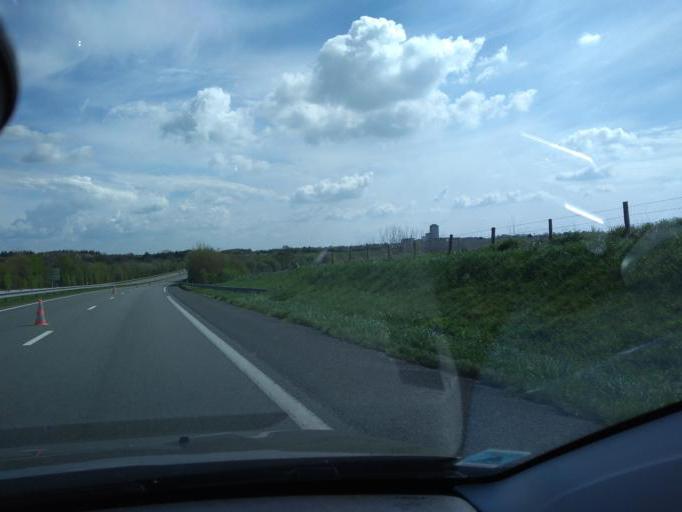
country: FR
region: Pays de la Loire
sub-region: Departement de Maine-et-Loire
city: Pouance
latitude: 47.7541
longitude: -1.1628
